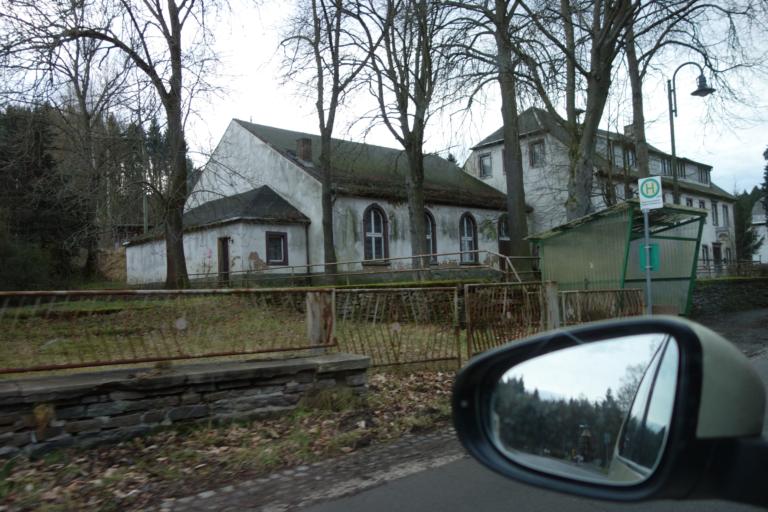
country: DE
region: Saxony
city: Leubsdorf
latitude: 50.8185
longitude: 13.1858
